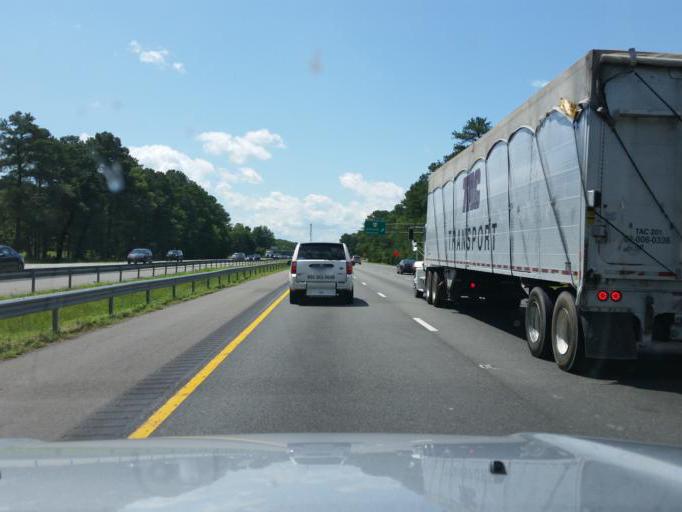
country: US
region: Virginia
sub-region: Hanover County
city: Ashland
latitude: 37.7655
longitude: -77.4612
